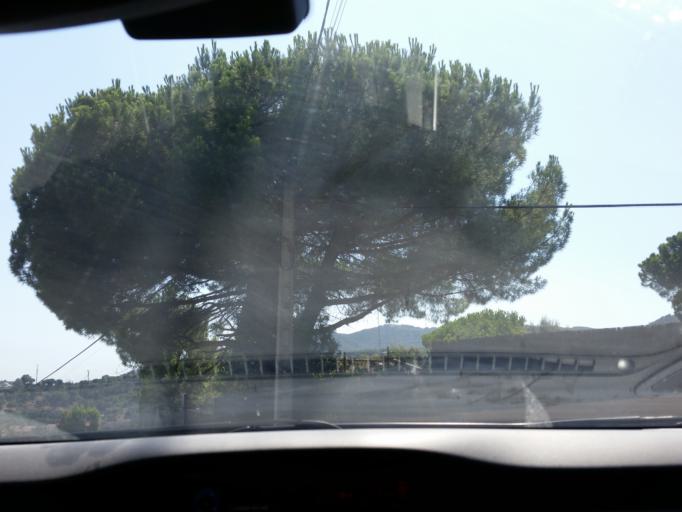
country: ES
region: Catalonia
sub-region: Provincia de Barcelona
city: Cabrils
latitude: 41.5317
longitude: 2.3702
